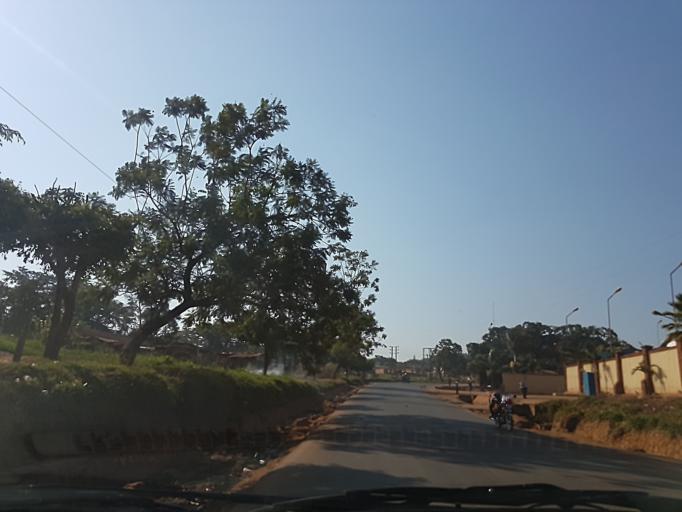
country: UG
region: Central Region
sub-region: Wakiso District
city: Kireka
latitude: 0.3349
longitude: 32.6164
